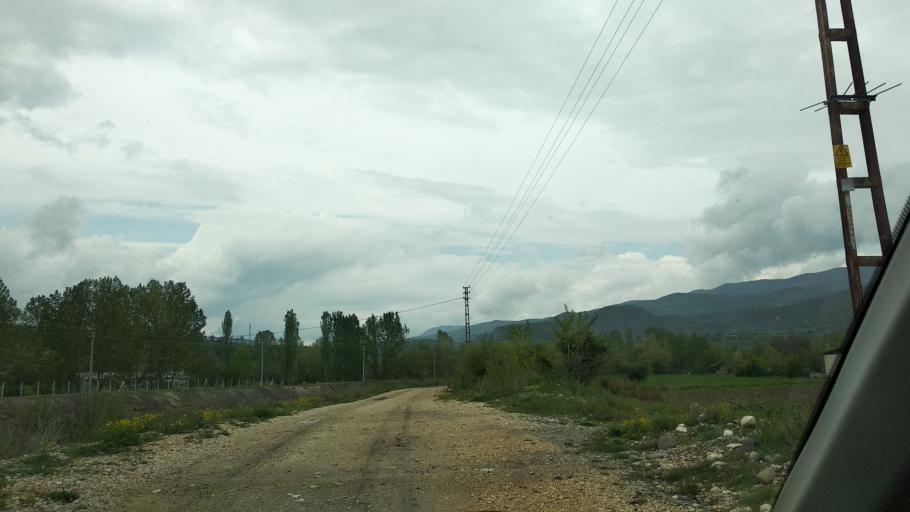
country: TR
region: Bolu
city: Seben
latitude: 40.4083
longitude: 31.5646
